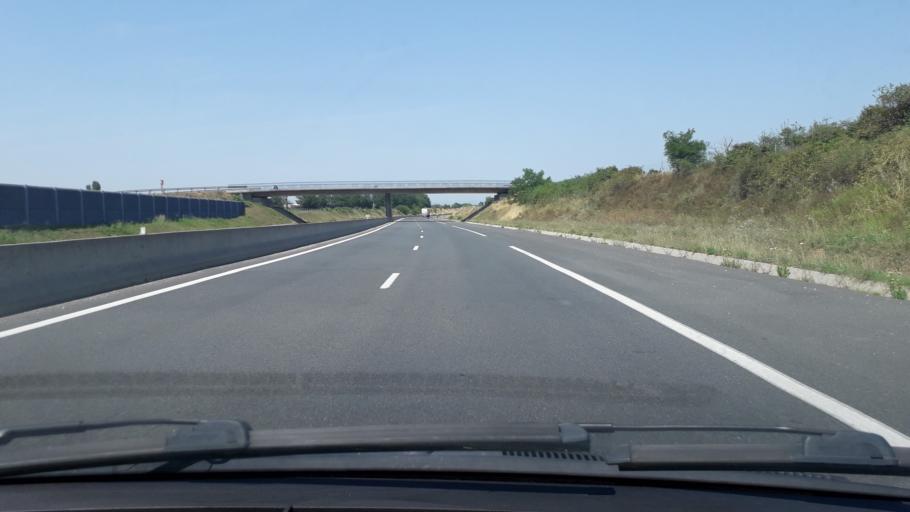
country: FR
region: Rhone-Alpes
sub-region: Departement du Rhone
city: Pusignan
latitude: 45.7668
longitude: 5.0685
